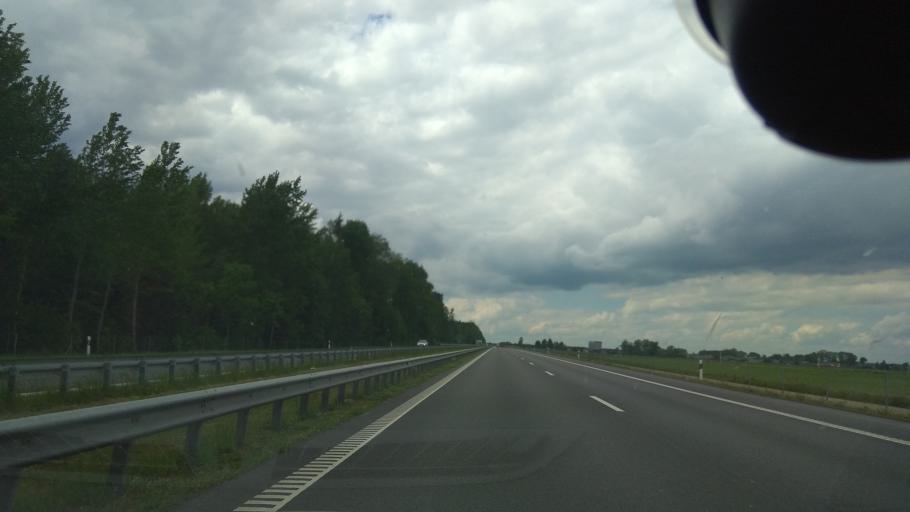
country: LT
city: Kazlu Ruda
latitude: 54.6745
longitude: 23.5573
